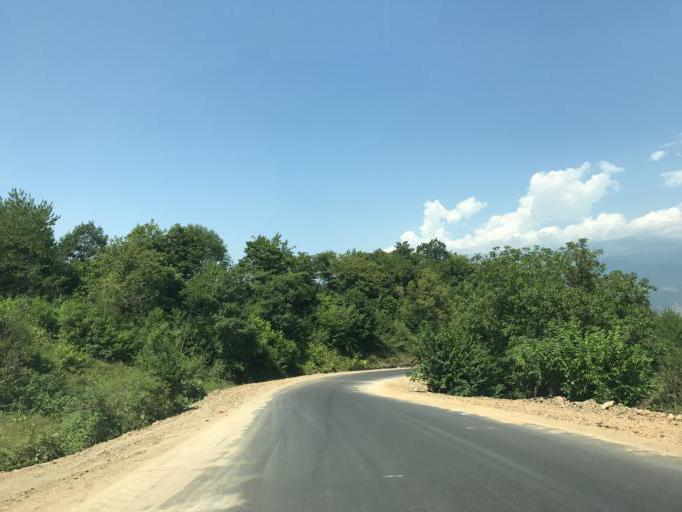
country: AZ
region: Tartar Rayon
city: Martakert
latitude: 40.1243
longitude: 46.6268
